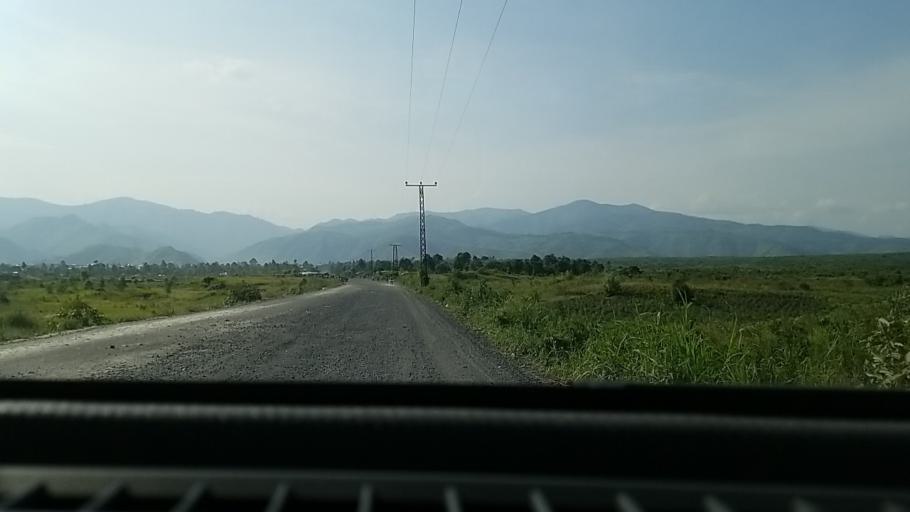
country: CD
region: Nord Kivu
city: Sake
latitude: -1.5802
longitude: 29.0790
